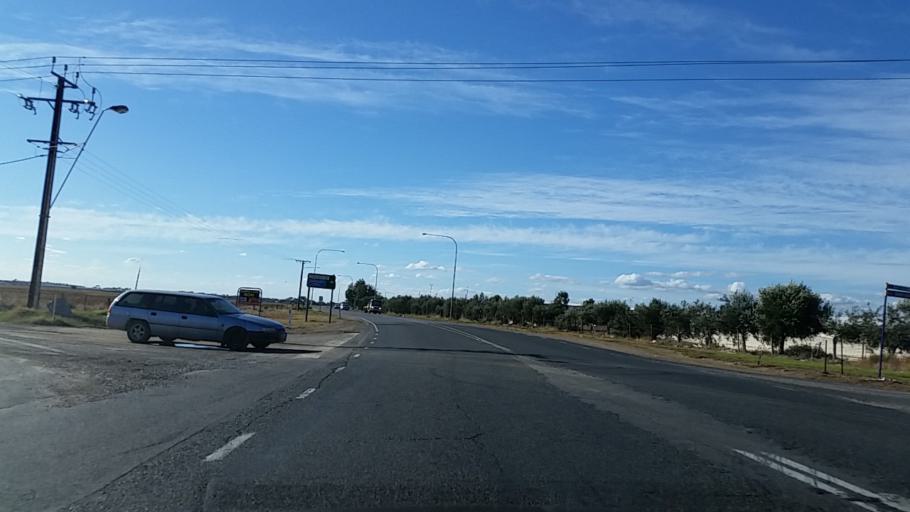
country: AU
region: South Australia
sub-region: Salisbury
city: Salisbury
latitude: -34.7228
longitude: 138.5975
